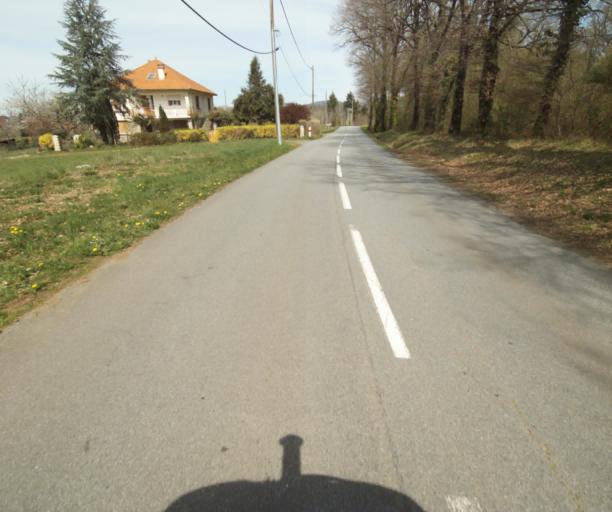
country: FR
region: Limousin
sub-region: Departement de la Correze
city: Correze
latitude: 45.3782
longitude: 1.8027
